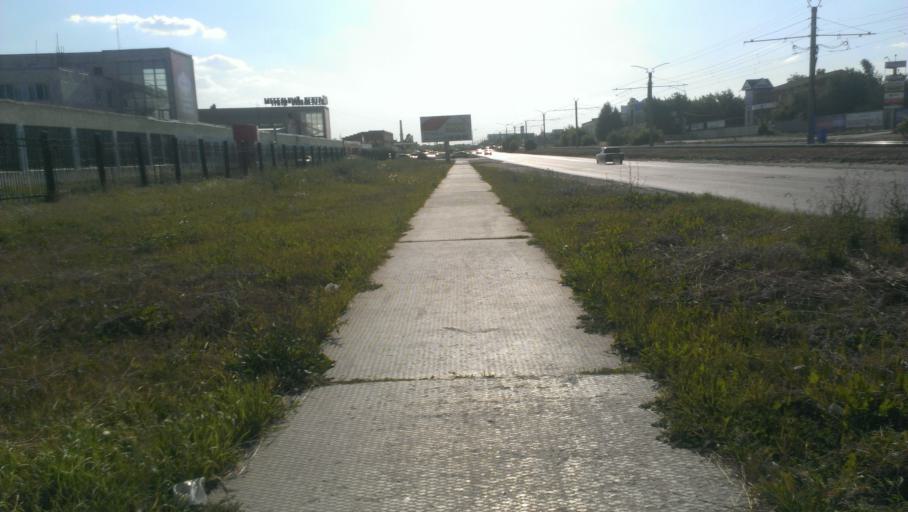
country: RU
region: Altai Krai
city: Novosilikatnyy
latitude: 53.3230
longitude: 83.6413
